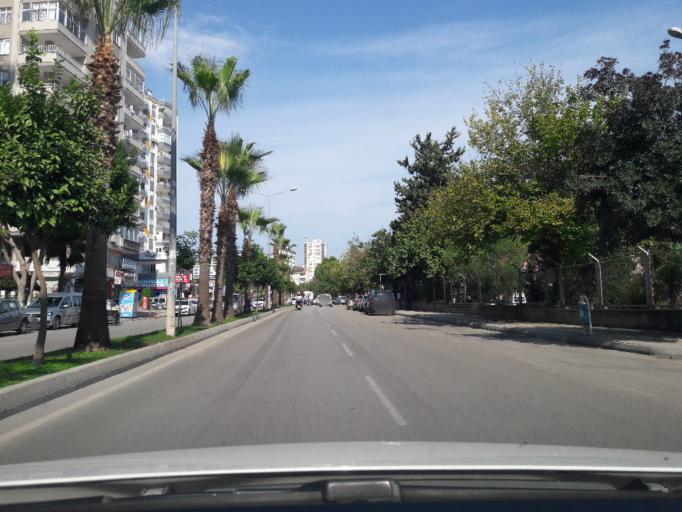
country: TR
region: Adana
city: Adana
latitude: 37.0177
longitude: 35.3215
